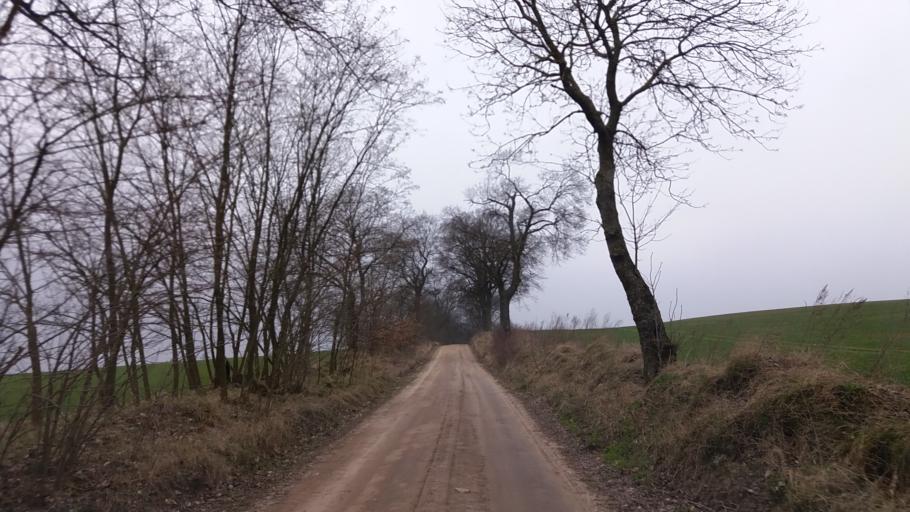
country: PL
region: West Pomeranian Voivodeship
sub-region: Powiat choszczenski
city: Choszczno
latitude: 53.1705
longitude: 15.3341
